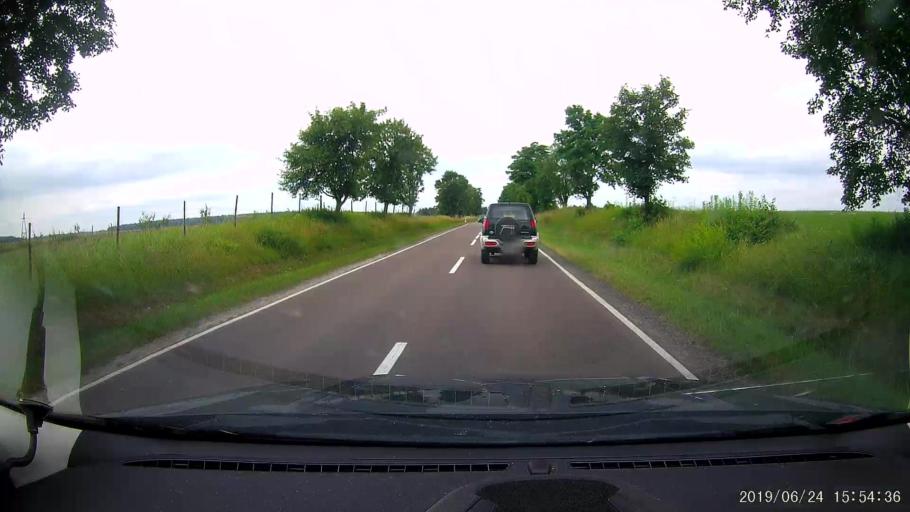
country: PL
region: Subcarpathian Voivodeship
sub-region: Powiat lubaczowski
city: Cieszanow
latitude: 50.2219
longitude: 23.1152
